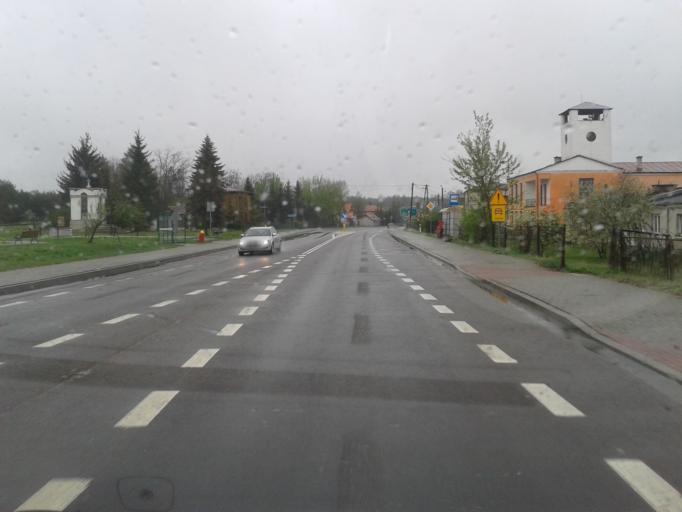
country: PL
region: Lublin Voivodeship
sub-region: Powiat tomaszowski
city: Belzec
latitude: 50.3820
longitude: 23.4407
